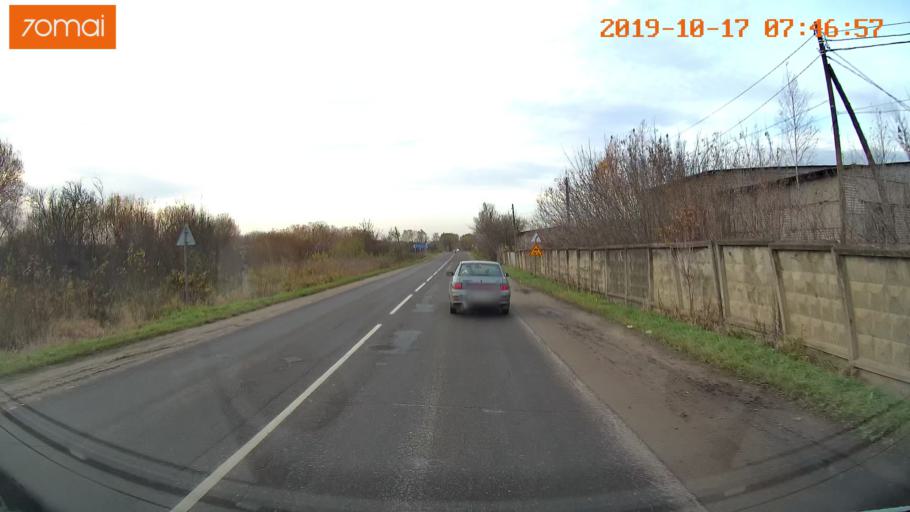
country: RU
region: Vladimir
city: Yur'yev-Pol'skiy
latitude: 56.4906
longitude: 39.6878
